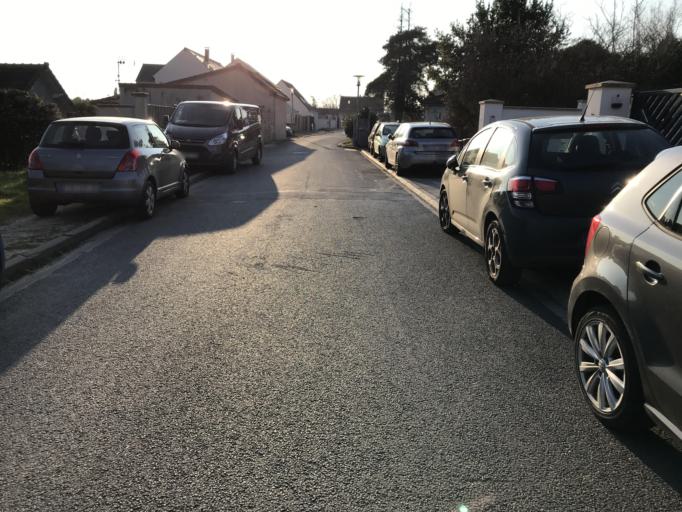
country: FR
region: Ile-de-France
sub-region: Departement de l'Essonne
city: Villejust
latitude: 48.6757
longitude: 2.2406
